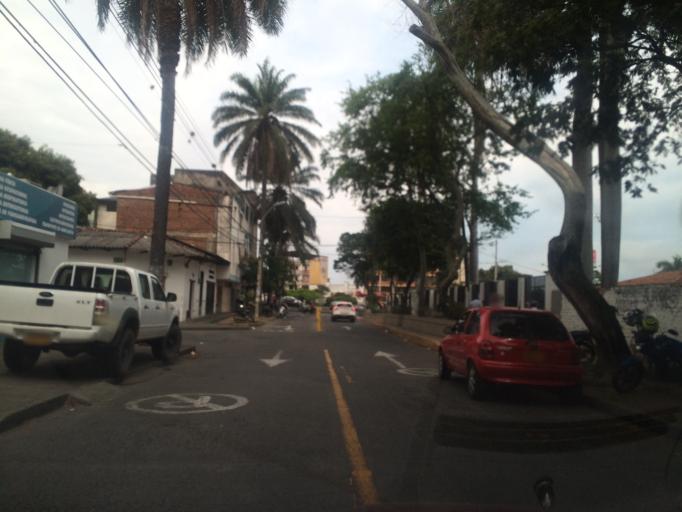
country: CO
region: Valle del Cauca
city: Cali
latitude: 3.4404
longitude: -76.5377
